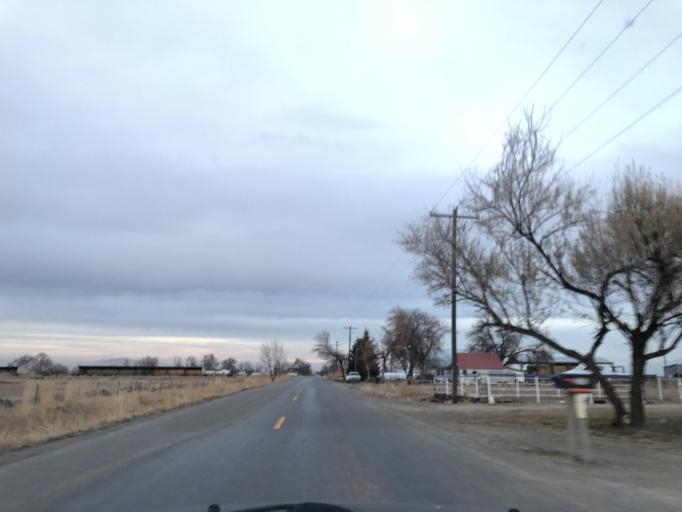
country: US
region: Utah
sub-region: Cache County
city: Benson
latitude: 41.7815
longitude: -111.9116
